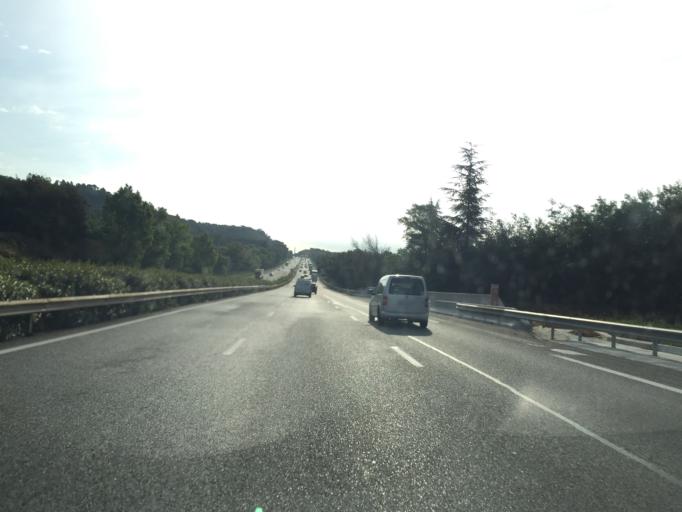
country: FR
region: Provence-Alpes-Cote d'Azur
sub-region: Departement des Alpes-Maritimes
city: Mandelieu-la-Napoule
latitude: 43.5357
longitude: 6.8893
